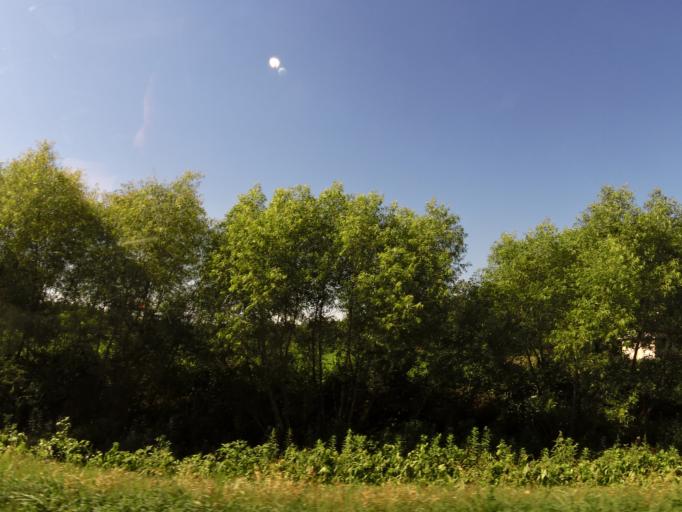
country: US
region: Arkansas
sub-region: Clay County
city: Piggott
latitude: 36.4293
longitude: -90.2766
